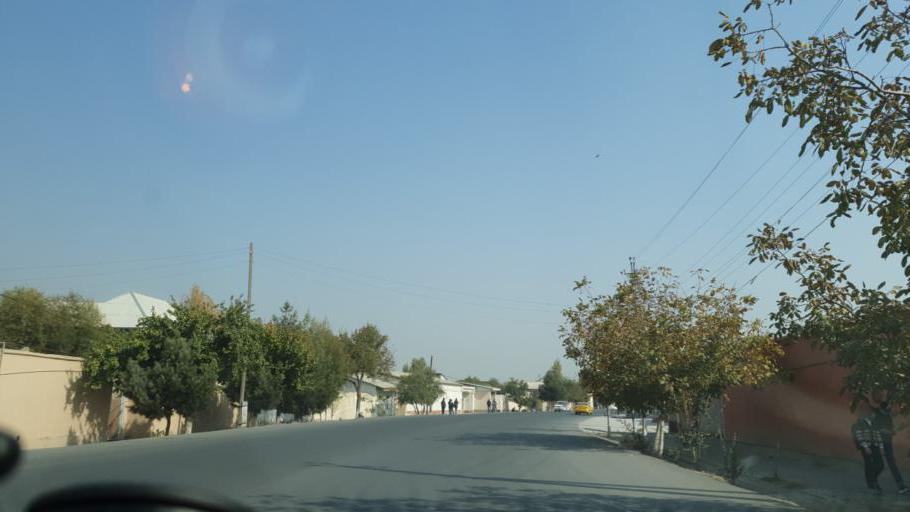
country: UZ
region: Fergana
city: Beshariq
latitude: 40.4358
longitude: 70.5959
